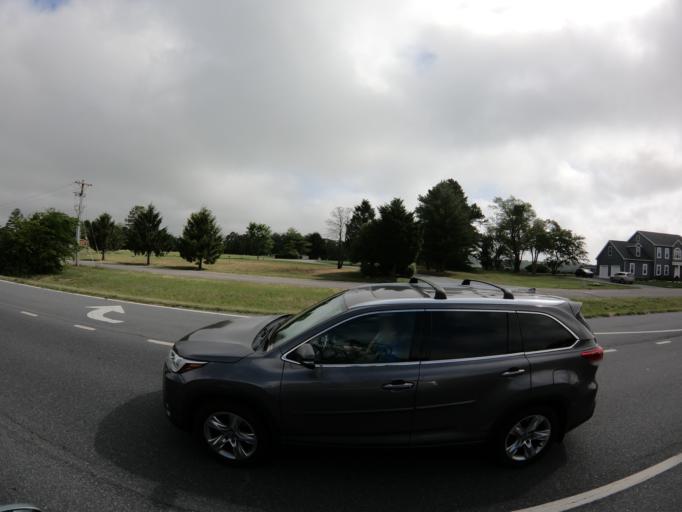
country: US
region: Delaware
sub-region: Sussex County
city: Milton
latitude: 38.7883
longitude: -75.2468
